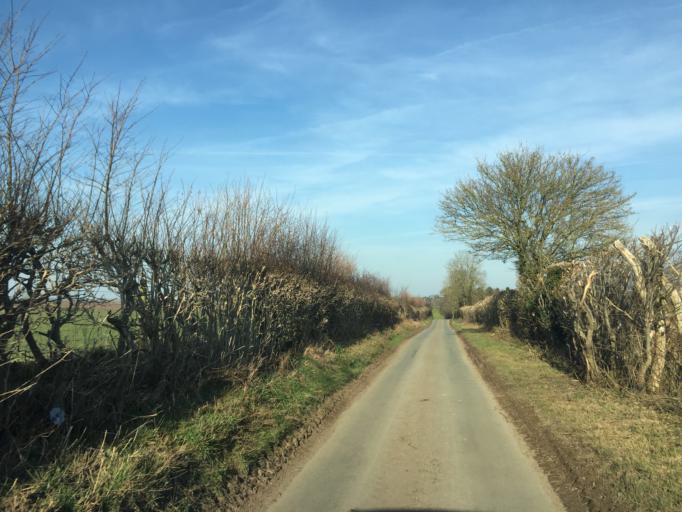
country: GB
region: England
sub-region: Shropshire
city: Bridgnorth
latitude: 52.5385
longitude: -2.4743
